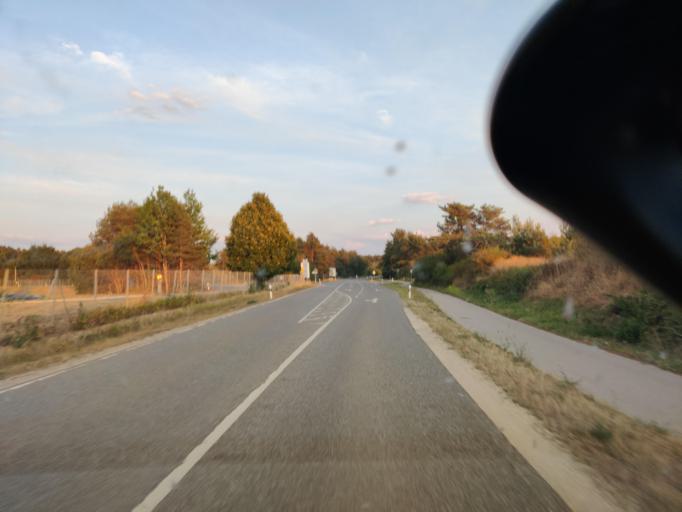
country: DE
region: Bavaria
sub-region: Regierungsbezirk Mittelfranken
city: Hilpoltstein
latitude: 49.1616
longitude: 11.1960
